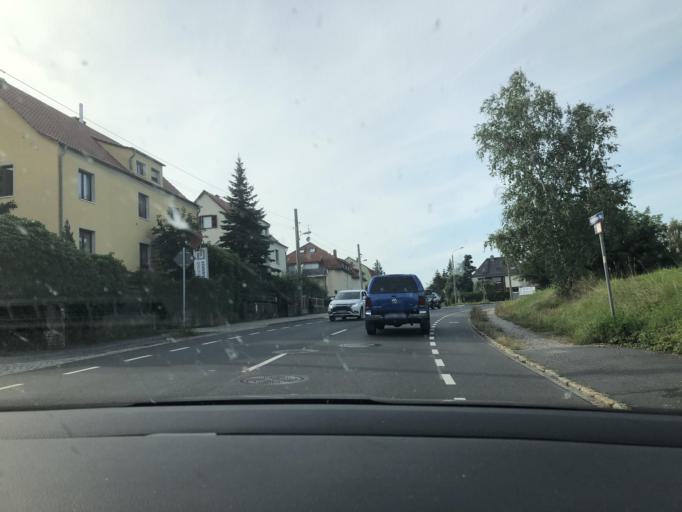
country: DE
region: Saxony
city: Albertstadt
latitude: 51.1126
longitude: 13.7285
